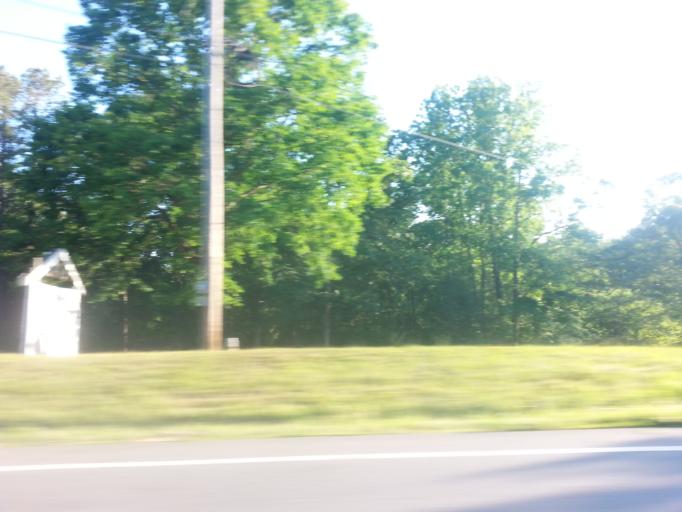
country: US
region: North Carolina
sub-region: Cherokee County
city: Murphy
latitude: 35.0181
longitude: -84.0897
